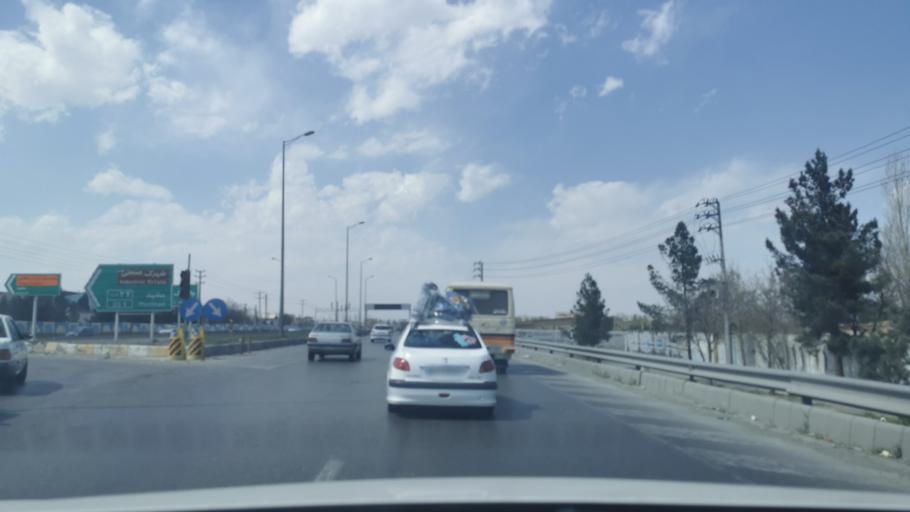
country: IR
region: Razavi Khorasan
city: Torqabeh
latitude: 36.4348
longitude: 59.4474
